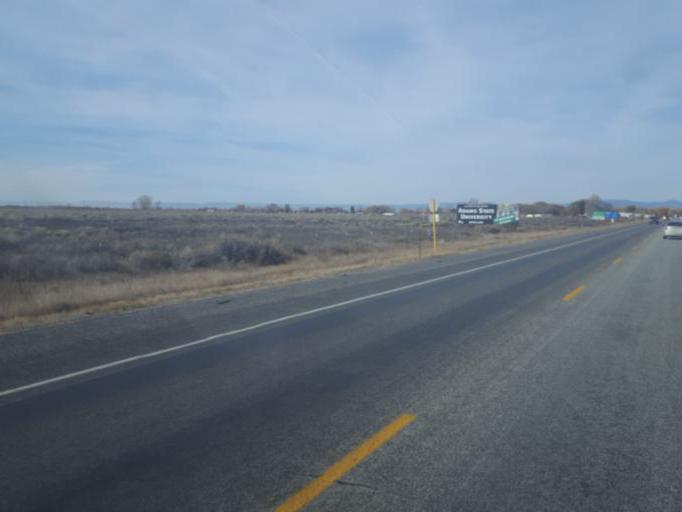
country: US
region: Colorado
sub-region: Alamosa County
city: Alamosa East
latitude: 37.4734
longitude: -105.8045
